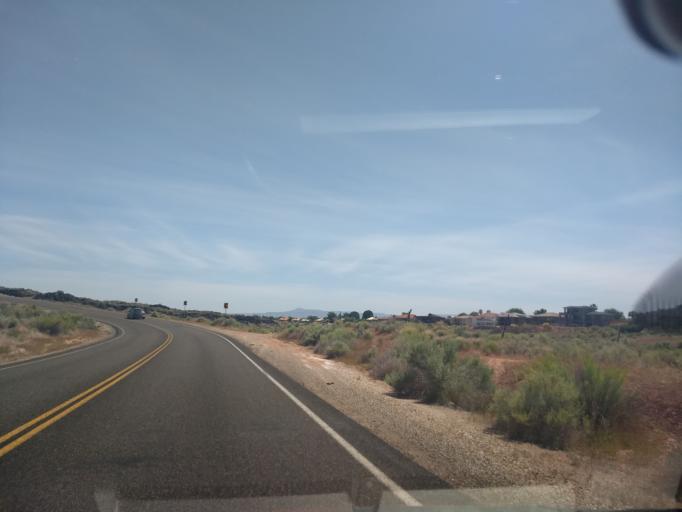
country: US
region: Utah
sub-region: Washington County
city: Santa Clara
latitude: 37.1450
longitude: -113.6521
